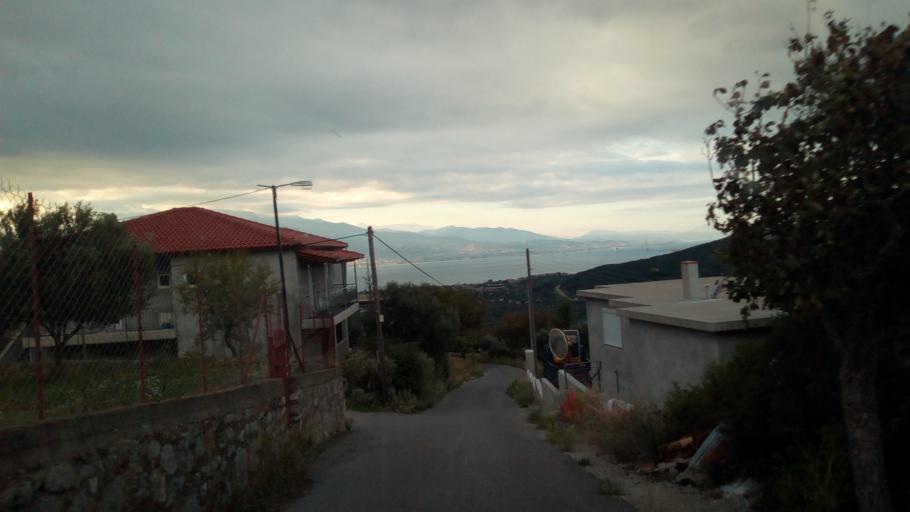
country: GR
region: West Greece
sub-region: Nomos Aitolias kai Akarnanias
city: Nafpaktos
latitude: 38.4051
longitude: 21.8008
